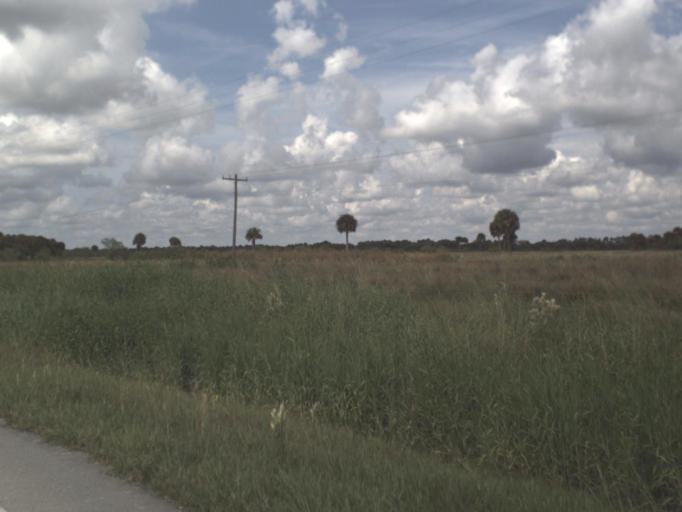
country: US
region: Florida
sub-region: Okeechobee County
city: Okeechobee
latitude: 27.2436
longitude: -80.9504
